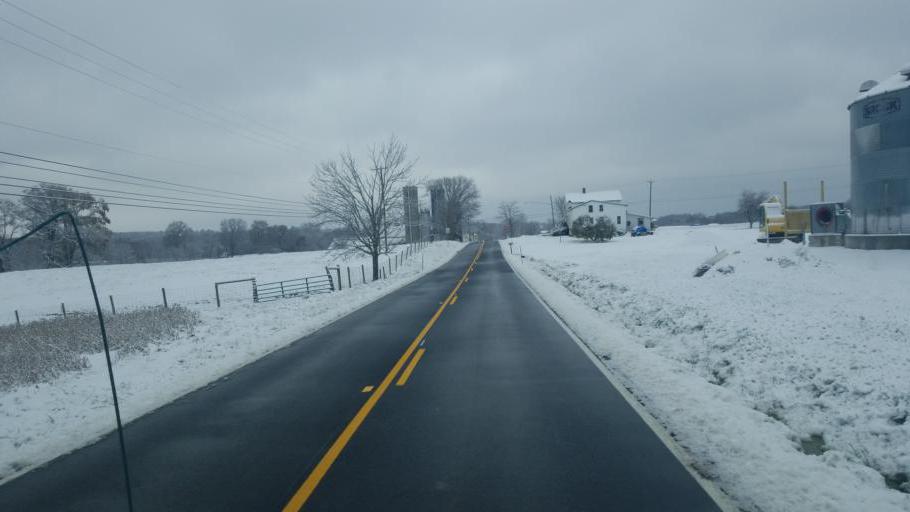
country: US
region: Ohio
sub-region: Portage County
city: Garrettsville
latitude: 41.3600
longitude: -81.0816
